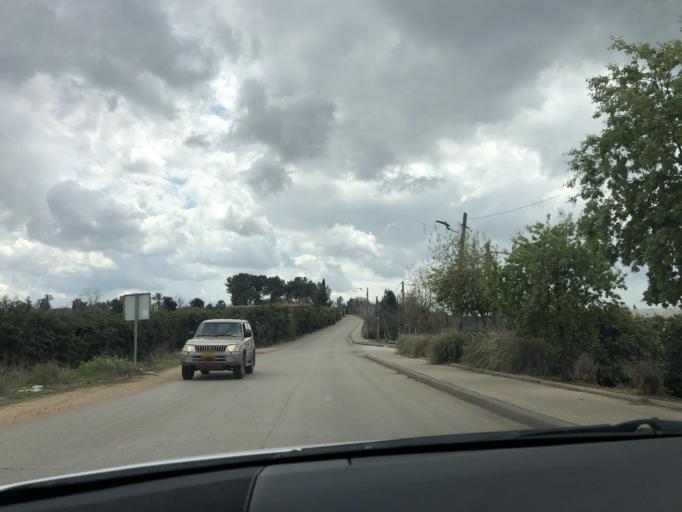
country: IL
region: Central District
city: Tel Mond
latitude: 32.2707
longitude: 34.9357
